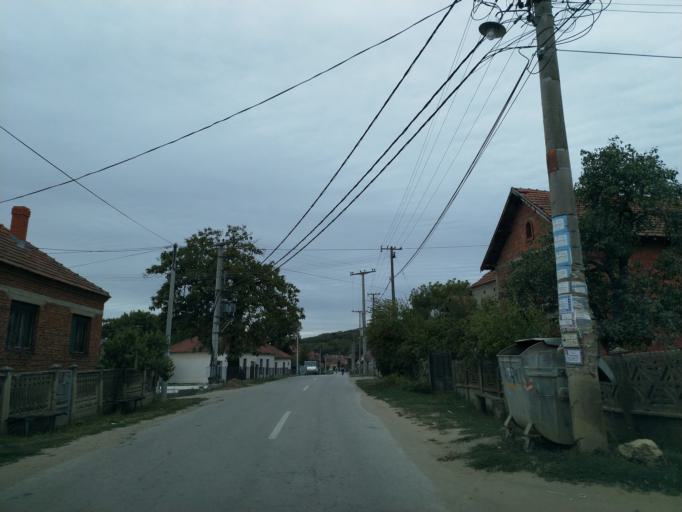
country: RS
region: Central Serbia
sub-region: Pomoravski Okrug
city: Cuprija
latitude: 43.8709
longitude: 21.3224
